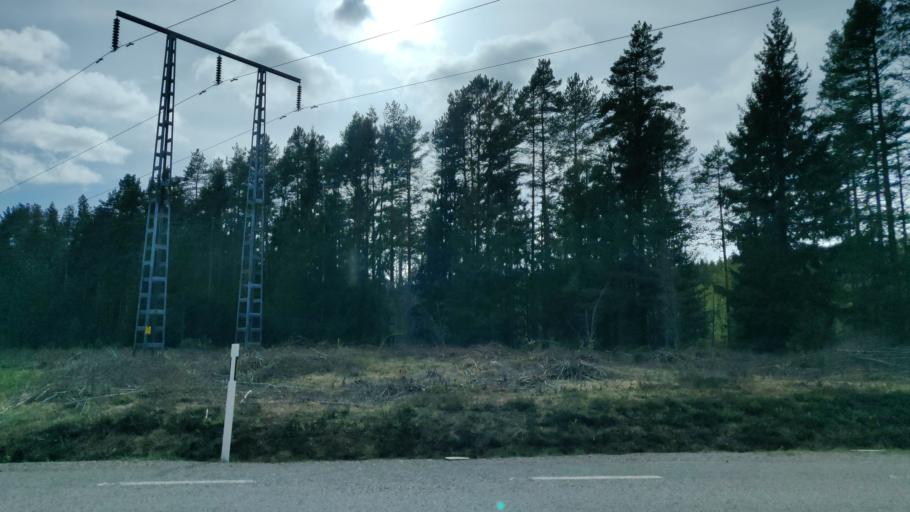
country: SE
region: Vaermland
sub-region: Forshaga Kommun
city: Deje
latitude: 59.5986
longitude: 13.4509
